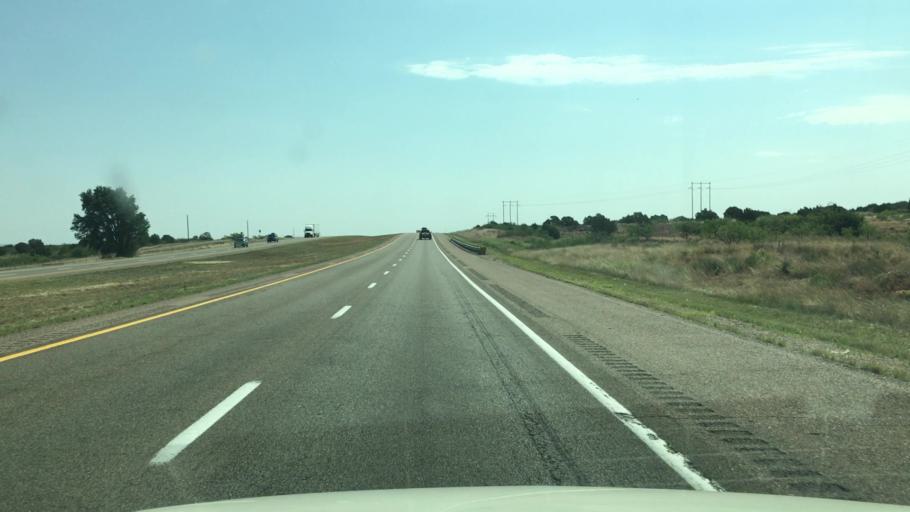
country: US
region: New Mexico
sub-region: Guadalupe County
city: Santa Rosa
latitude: 35.0484
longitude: -104.3670
